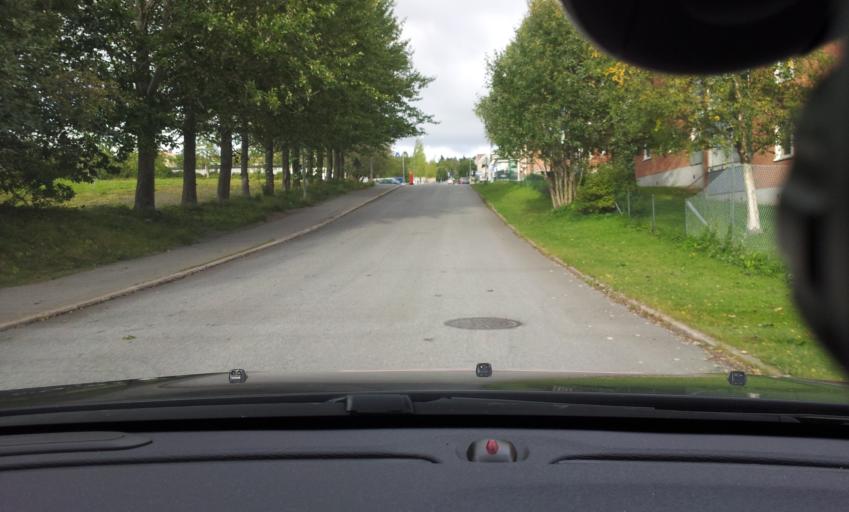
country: SE
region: Jaemtland
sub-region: OEstersunds Kommun
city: Ostersund
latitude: 63.1605
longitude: 14.6557
